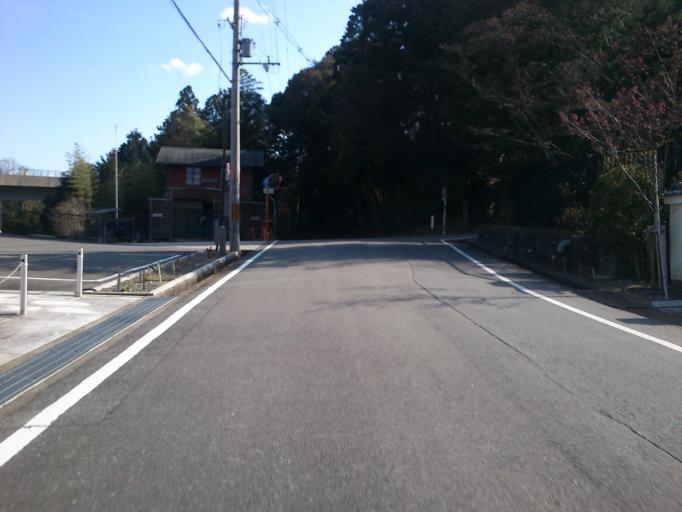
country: JP
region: Kyoto
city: Yawata
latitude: 34.9107
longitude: 135.6531
